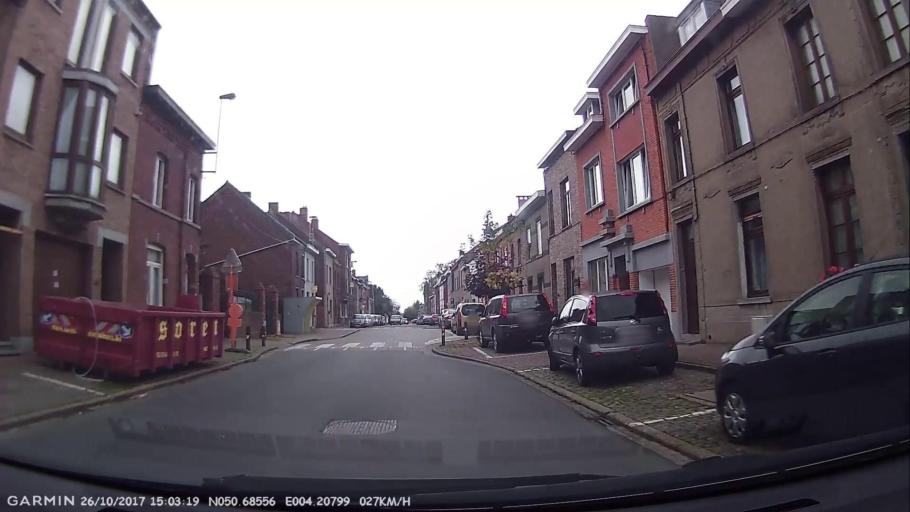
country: BE
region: Wallonia
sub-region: Province du Brabant Wallon
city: Tubize
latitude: 50.6856
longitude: 4.2080
